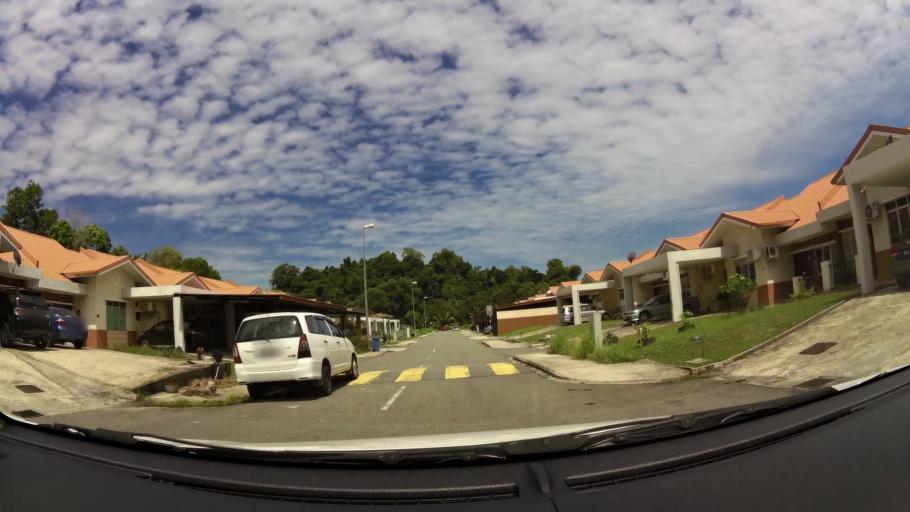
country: BN
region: Brunei and Muara
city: Bandar Seri Begawan
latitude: 4.9913
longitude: 115.0069
